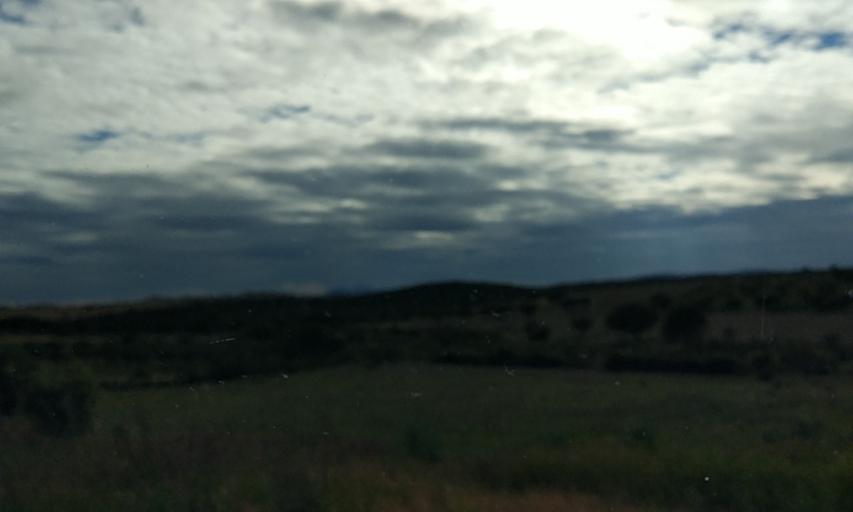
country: ES
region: Extremadura
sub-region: Provincia de Caceres
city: Perales del Puerto
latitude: 40.1125
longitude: -6.6708
